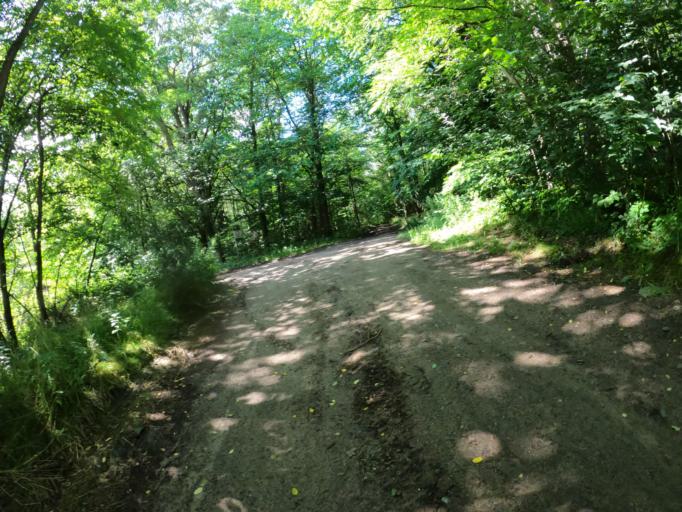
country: PL
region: West Pomeranian Voivodeship
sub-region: Powiat bialogardzki
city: Tychowo
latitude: 54.0038
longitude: 16.3681
